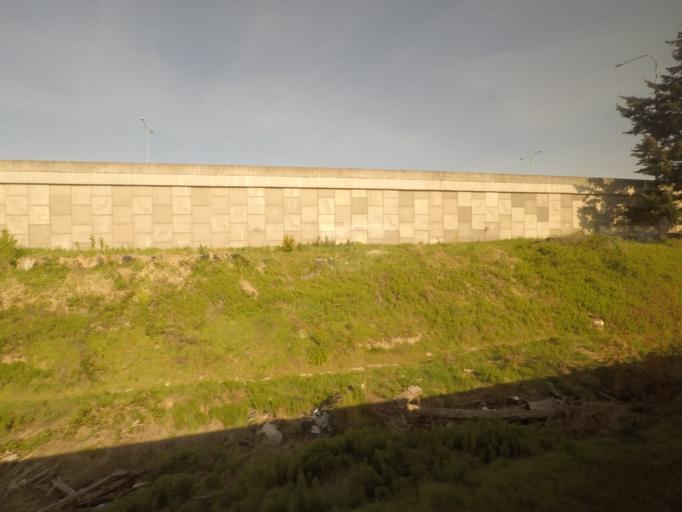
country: US
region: Washington
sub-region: Snohomish County
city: Everett
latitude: 47.9736
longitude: -122.1906
